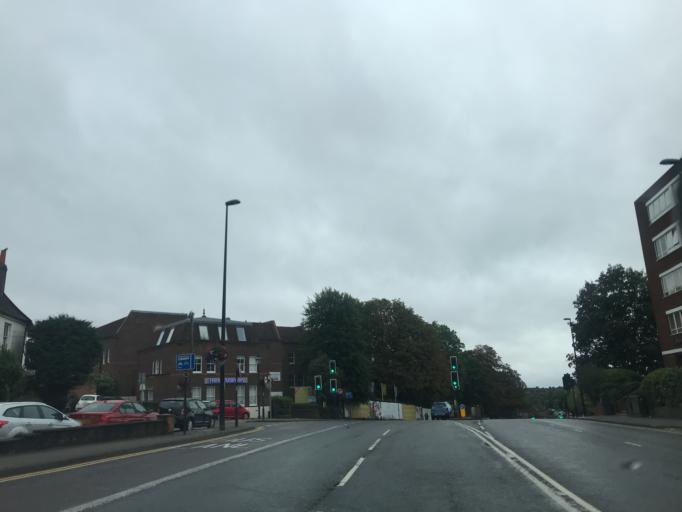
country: GB
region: England
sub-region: Buckinghamshire
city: Aylesbury
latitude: 51.8191
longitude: -0.8165
